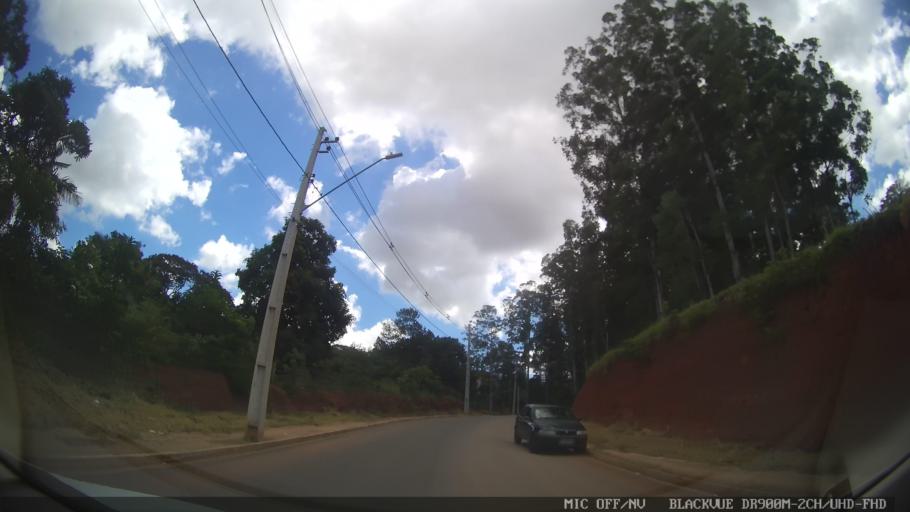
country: BR
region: Minas Gerais
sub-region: Extrema
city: Extrema
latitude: -22.8663
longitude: -46.3337
